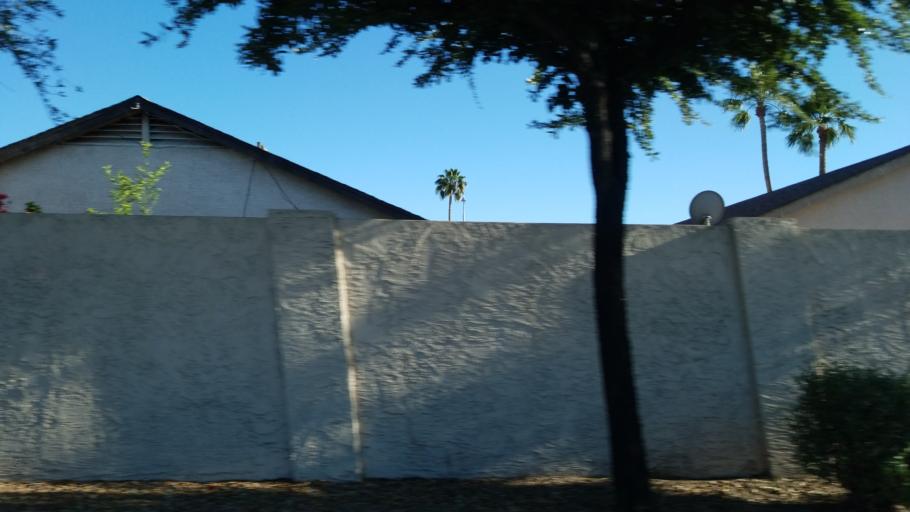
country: US
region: Arizona
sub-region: Maricopa County
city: Glendale
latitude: 33.5672
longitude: -112.1959
